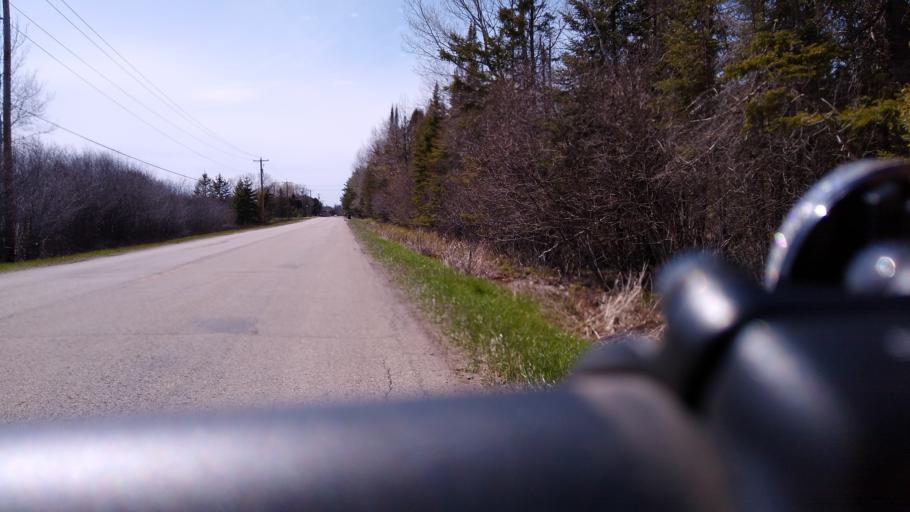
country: US
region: Michigan
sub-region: Delta County
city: Escanaba
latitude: 45.7353
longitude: -87.1797
